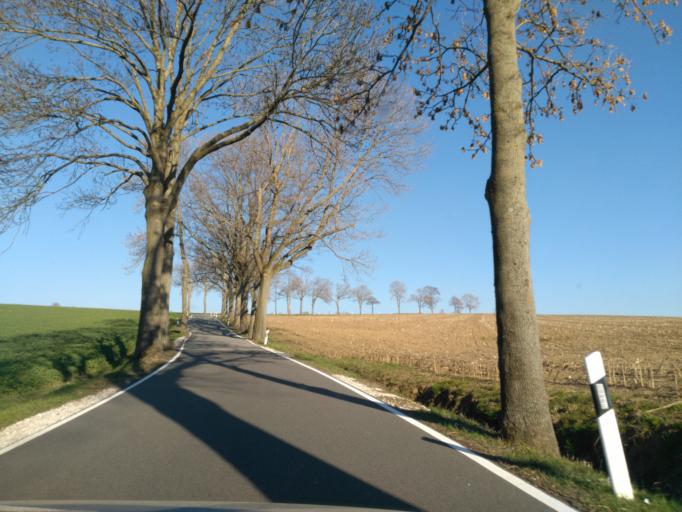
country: DE
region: Saxony
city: Schlettau
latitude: 50.5425
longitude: 12.9737
